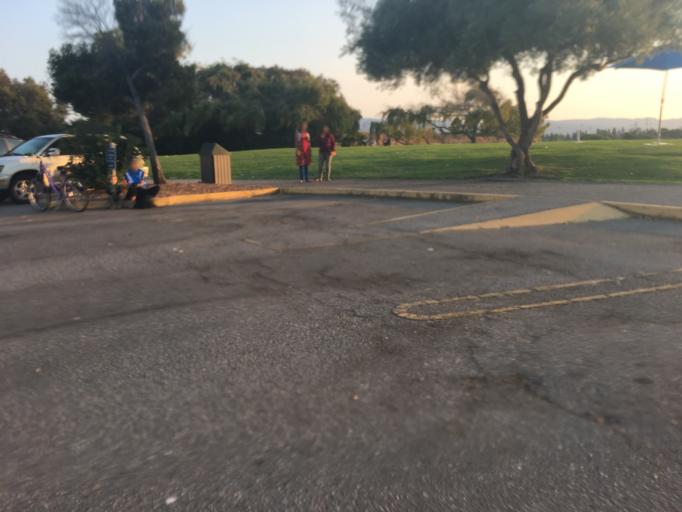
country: US
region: California
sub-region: Santa Clara County
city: Mountain View
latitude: 37.4323
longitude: -122.0881
